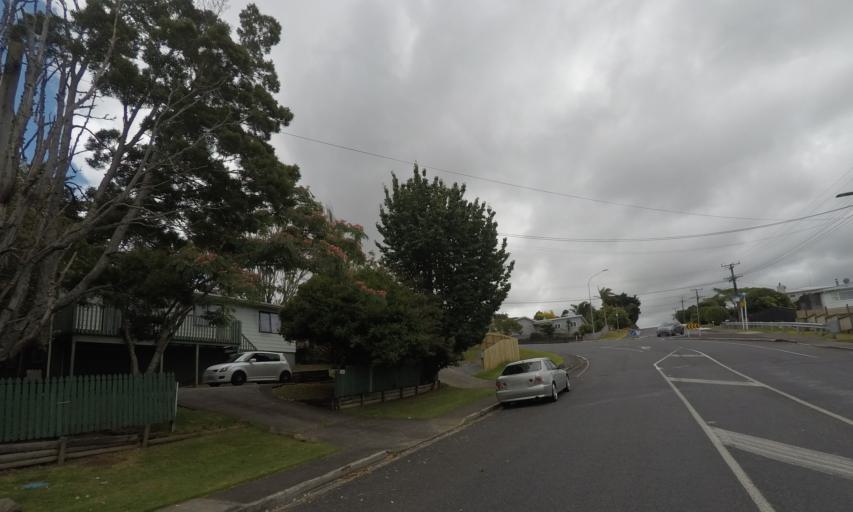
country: NZ
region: Northland
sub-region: Whangarei
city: Whangarei
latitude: -35.6772
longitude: 174.3130
